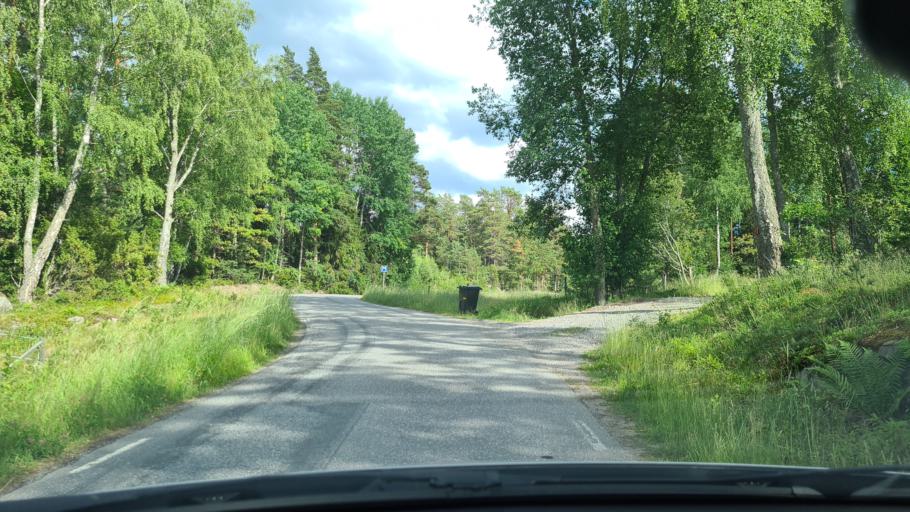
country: SE
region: Stockholm
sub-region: Vaxholms Kommun
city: Vaxholm
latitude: 59.4134
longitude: 18.4425
